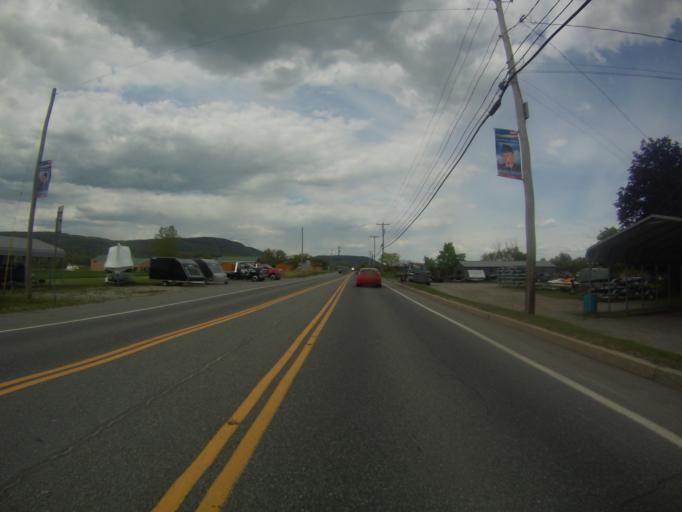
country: US
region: New York
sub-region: Essex County
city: Ticonderoga
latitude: 43.8608
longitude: -73.4377
